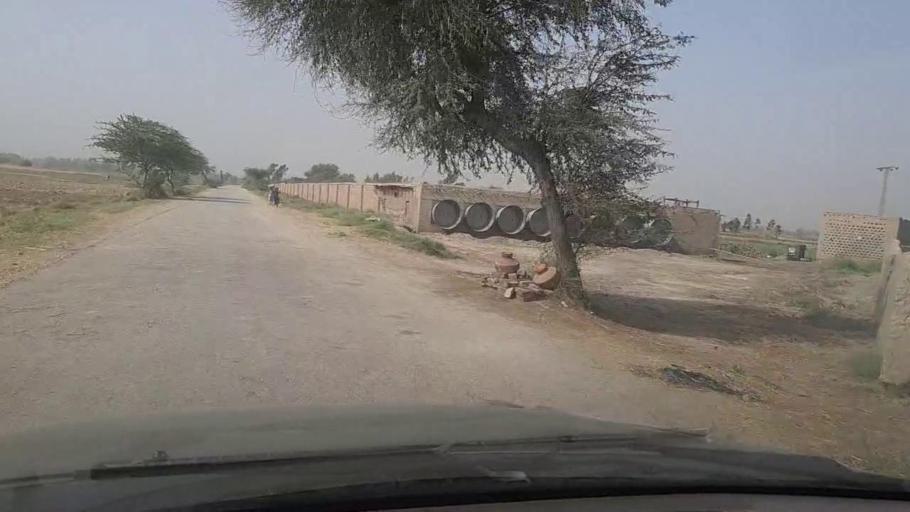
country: PK
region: Sindh
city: Shikarpur
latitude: 27.9214
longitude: 68.6117
